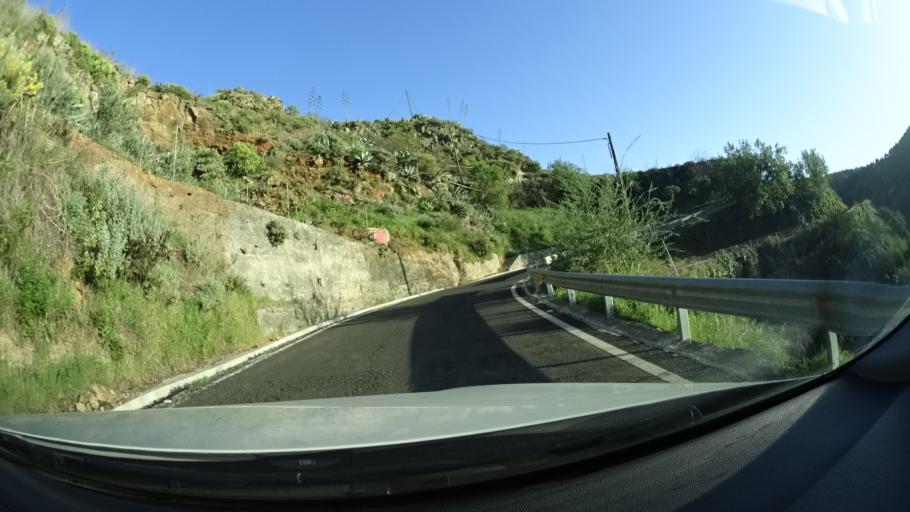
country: ES
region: Canary Islands
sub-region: Provincia de Las Palmas
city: Artenara
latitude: 28.0341
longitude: -15.6697
